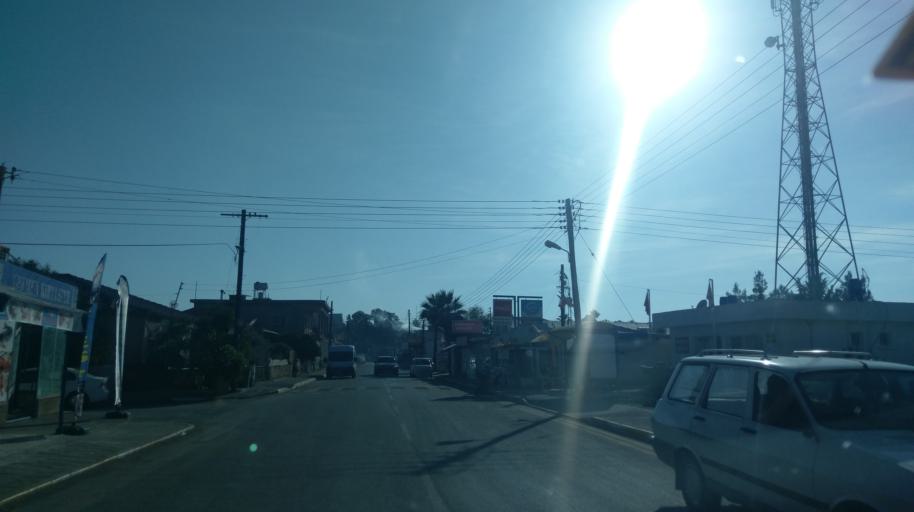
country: CY
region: Larnaka
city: Pergamos
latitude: 35.0407
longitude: 33.7076
